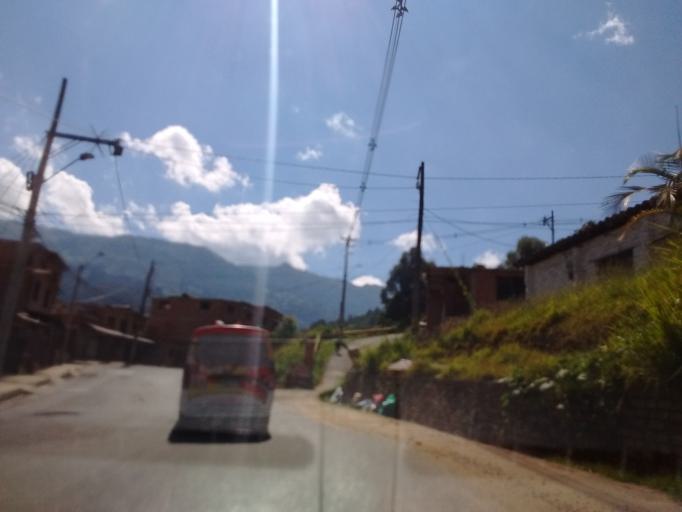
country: CO
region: Antioquia
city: Medellin
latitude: 6.2280
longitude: -75.5330
